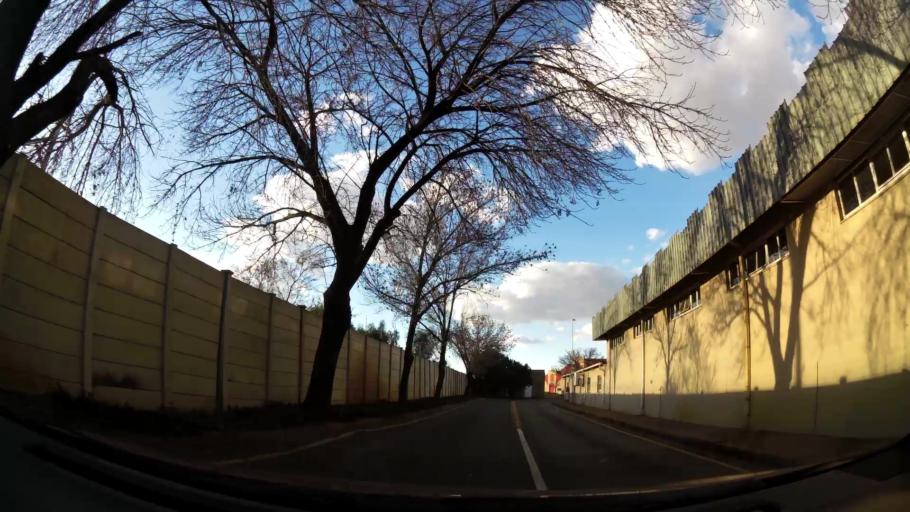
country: ZA
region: North-West
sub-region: Dr Kenneth Kaunda District Municipality
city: Potchefstroom
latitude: -26.6854
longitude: 27.0917
